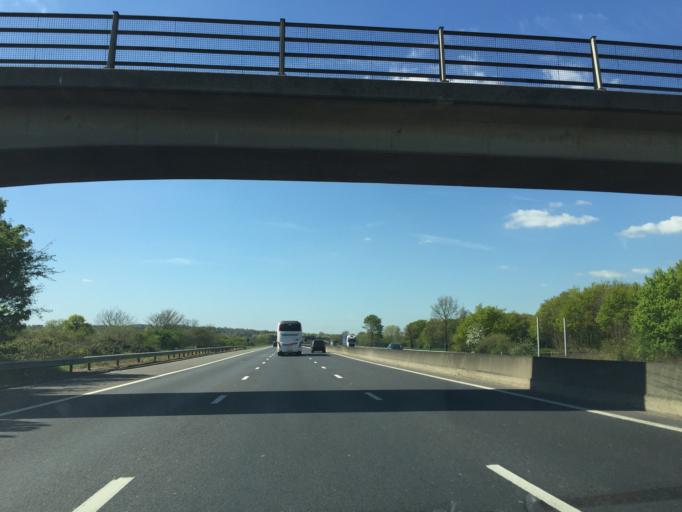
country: GB
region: England
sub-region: Essex
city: Theydon Bois
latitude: 51.6537
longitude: 0.1030
